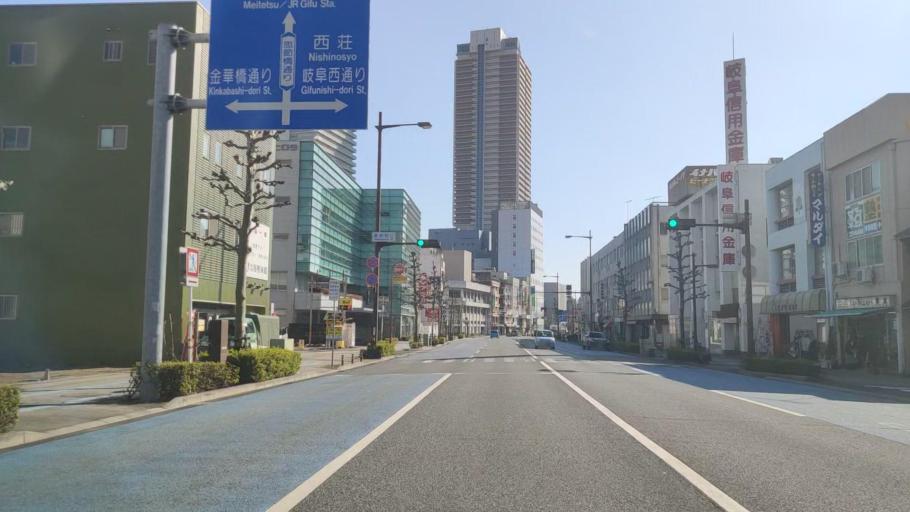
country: JP
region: Gifu
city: Gifu-shi
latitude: 35.4141
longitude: 136.7535
